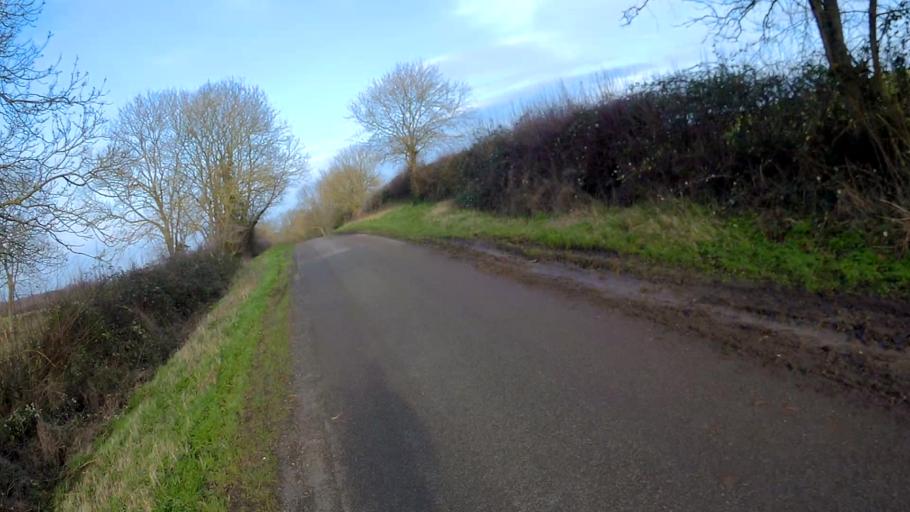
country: GB
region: England
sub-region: Lincolnshire
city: Bourne
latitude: 52.7448
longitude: -0.4183
